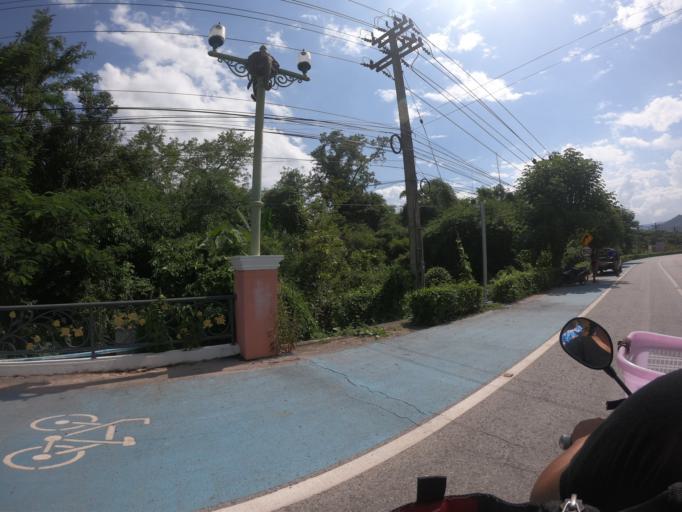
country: TH
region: Nakhon Nayok
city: Nakhon Nayok
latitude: 14.3154
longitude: 101.3124
